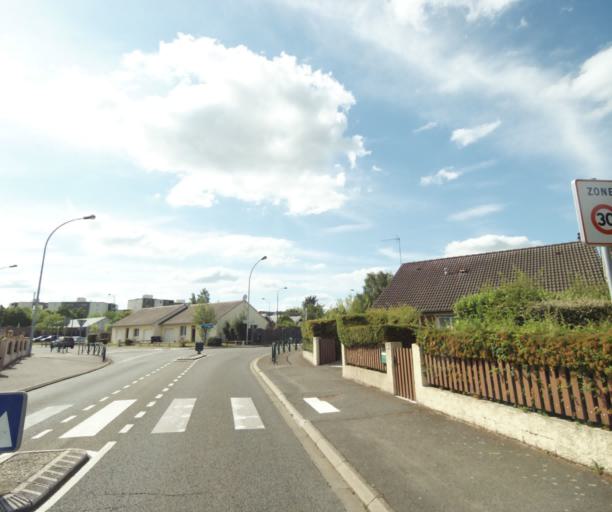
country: FR
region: Centre
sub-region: Departement d'Eure-et-Loir
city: Luce
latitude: 48.4326
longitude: 1.4506
